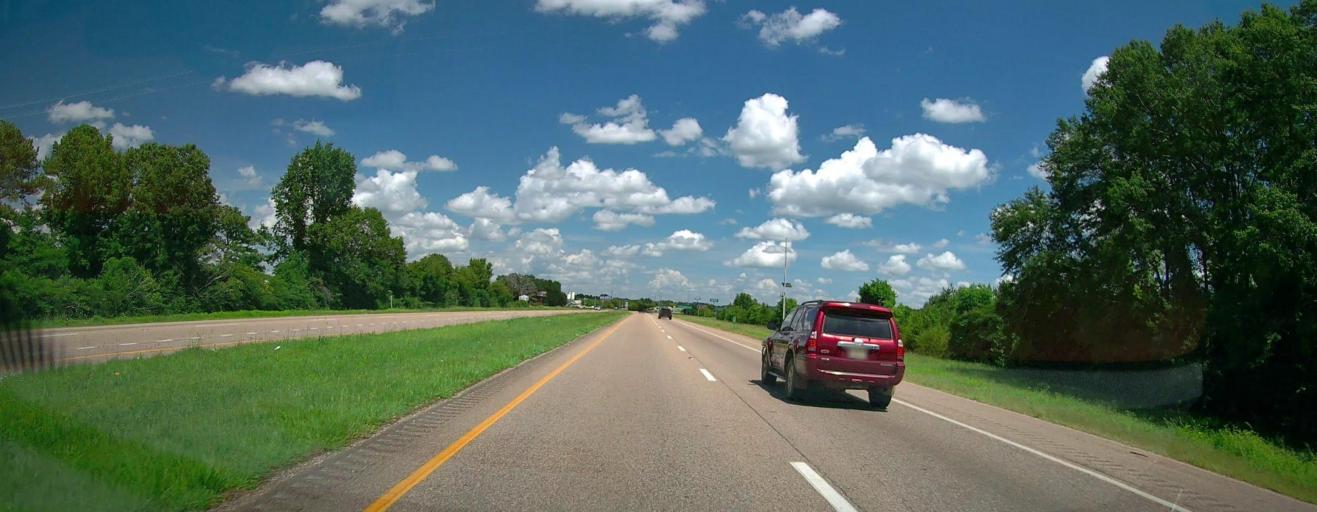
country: US
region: Alabama
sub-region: Montgomery County
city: Montgomery
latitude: 32.4219
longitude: -86.2406
